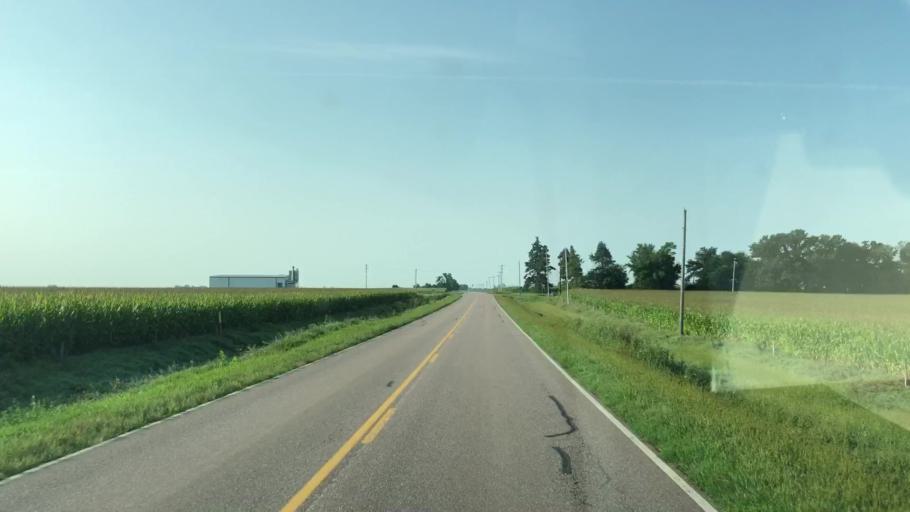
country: US
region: Iowa
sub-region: Lyon County
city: George
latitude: 43.2316
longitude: -96.0008
